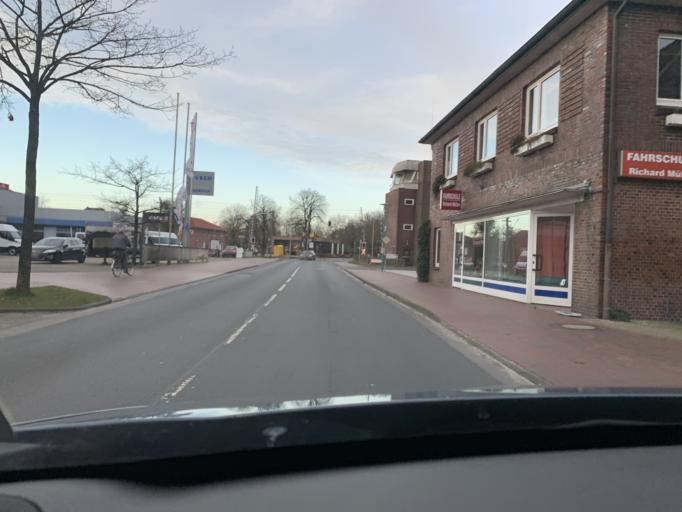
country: DE
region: Lower Saxony
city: Westerstede
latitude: 53.2018
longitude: 7.8848
